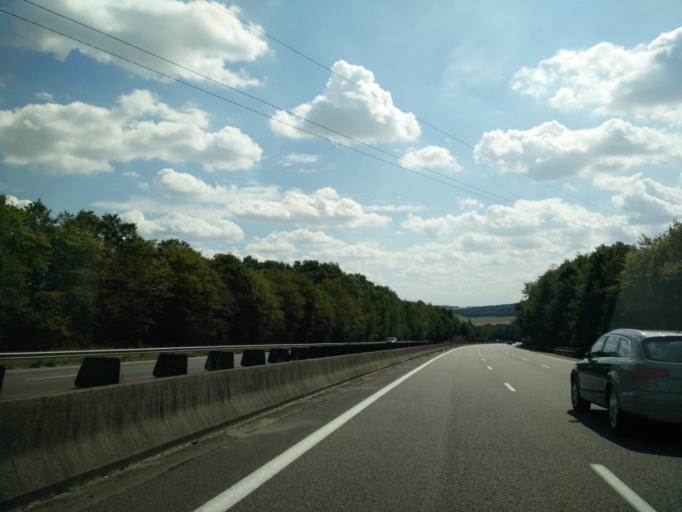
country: FR
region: Ile-de-France
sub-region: Departement des Yvelines
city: Rosny-sur-Seine
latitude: 49.0002
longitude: 1.6108
